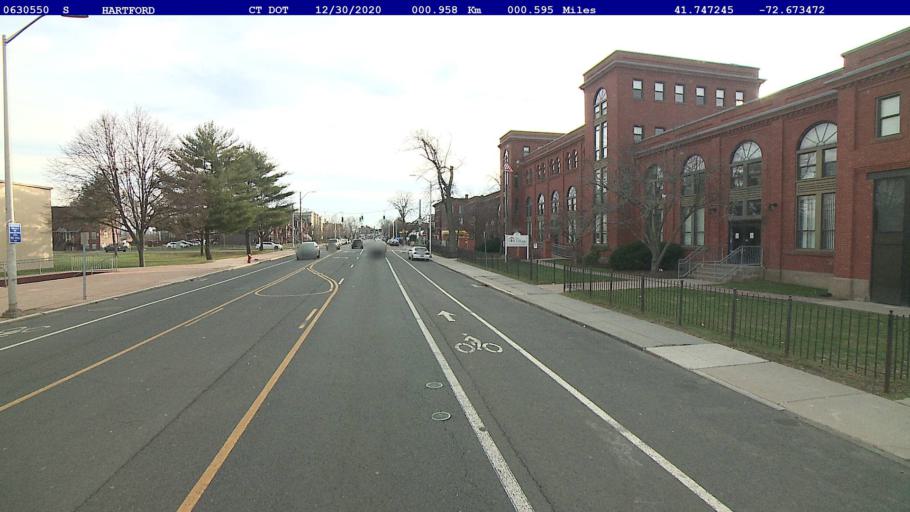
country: US
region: Connecticut
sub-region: Hartford County
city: Hartford
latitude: 41.7473
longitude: -72.6735
